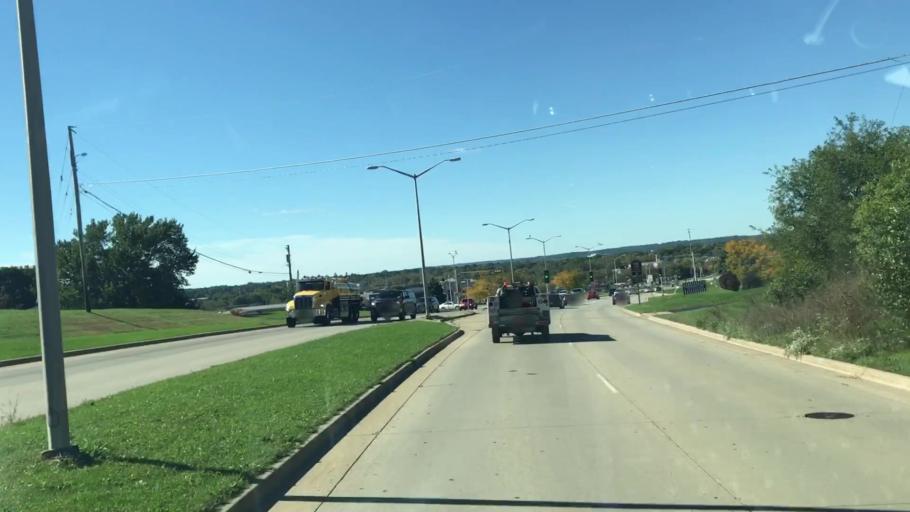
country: US
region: Wisconsin
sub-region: Waukesha County
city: Waukesha
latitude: 43.0230
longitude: -88.1958
